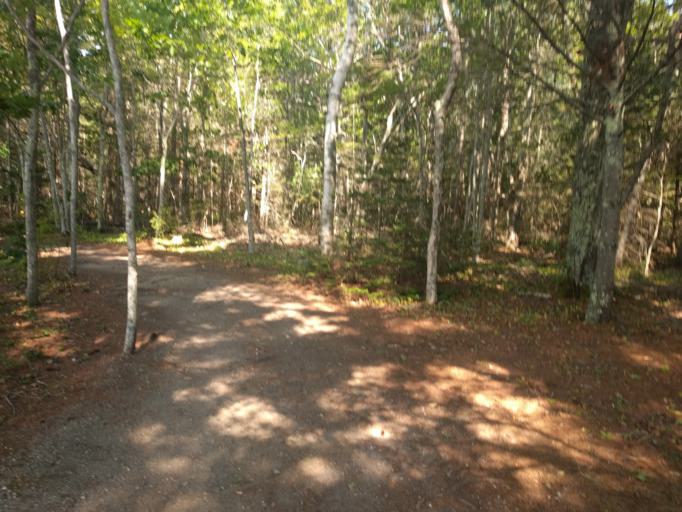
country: US
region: Maine
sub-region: Waldo County
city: Belfast
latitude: 44.4286
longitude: -68.9461
